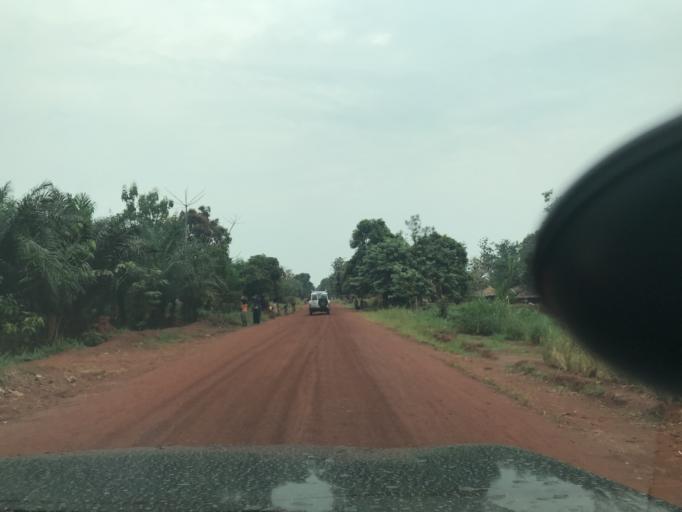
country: CD
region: Equateur
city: Gemena
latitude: 3.2178
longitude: 19.7830
